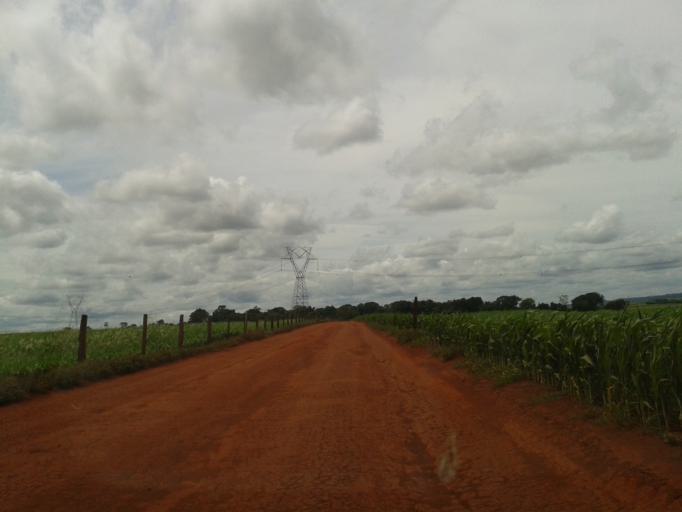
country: BR
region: Minas Gerais
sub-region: Centralina
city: Centralina
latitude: -18.5851
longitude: -49.2639
